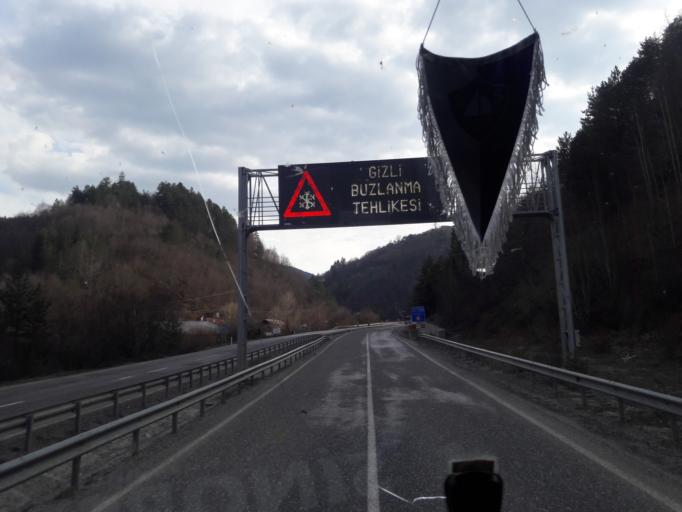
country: TR
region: Kastamonu
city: Kuzyaka
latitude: 41.1446
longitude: 33.7802
